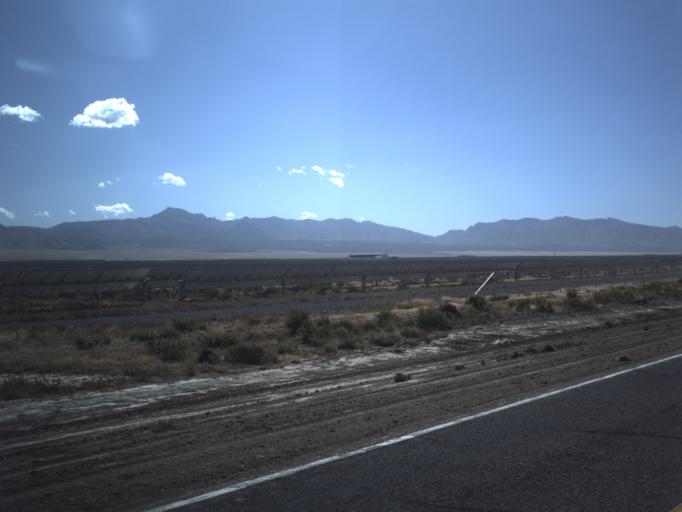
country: US
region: Utah
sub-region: Beaver County
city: Milford
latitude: 38.5097
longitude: -112.9912
